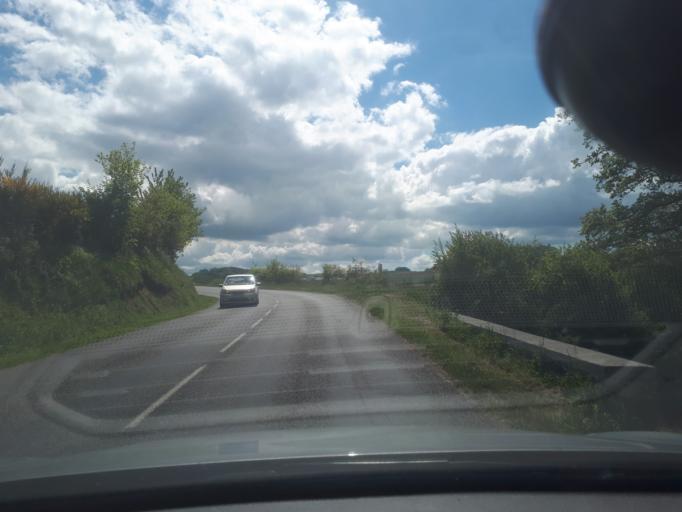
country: FR
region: Rhone-Alpes
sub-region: Departement du Rhone
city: Saint-Martin-en-Haut
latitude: 45.6736
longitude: 4.5515
